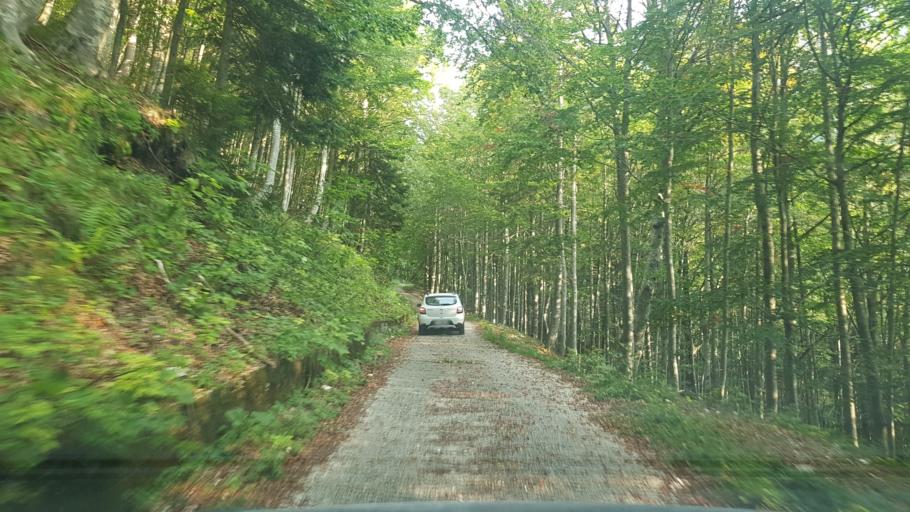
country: SI
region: Bovec
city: Bovec
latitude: 46.4108
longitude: 13.5087
